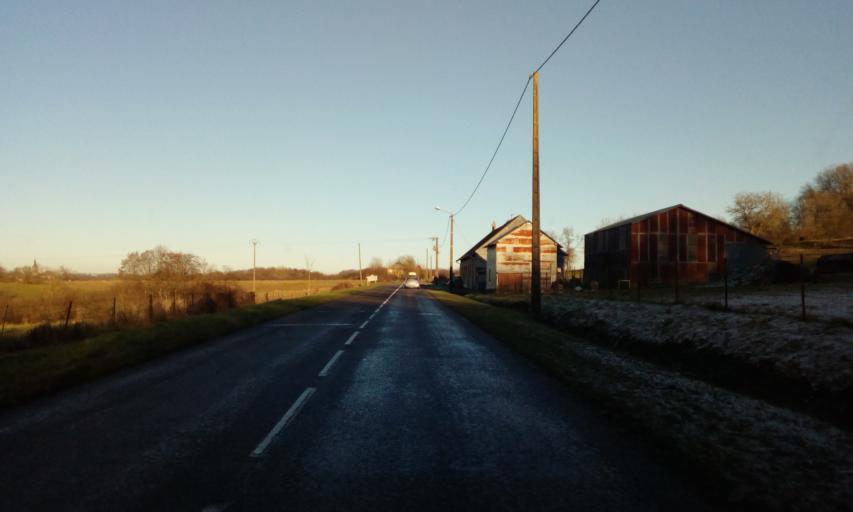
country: FR
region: Picardie
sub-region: Departement de l'Aisne
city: Rozoy-sur-Serre
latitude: 49.7295
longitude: 4.2760
